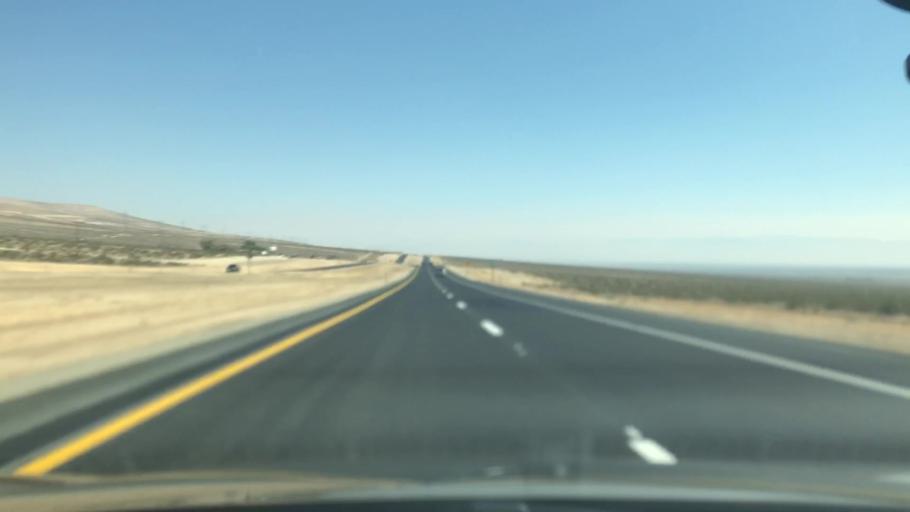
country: US
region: California
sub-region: Kern County
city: Inyokern
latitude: 35.6155
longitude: -117.8957
